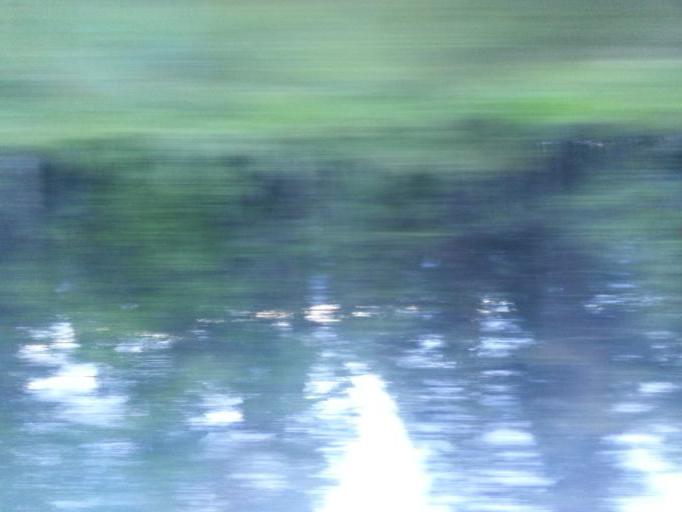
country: NO
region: Oppland
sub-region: Dovre
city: Dombas
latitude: 62.1104
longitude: 9.1100
